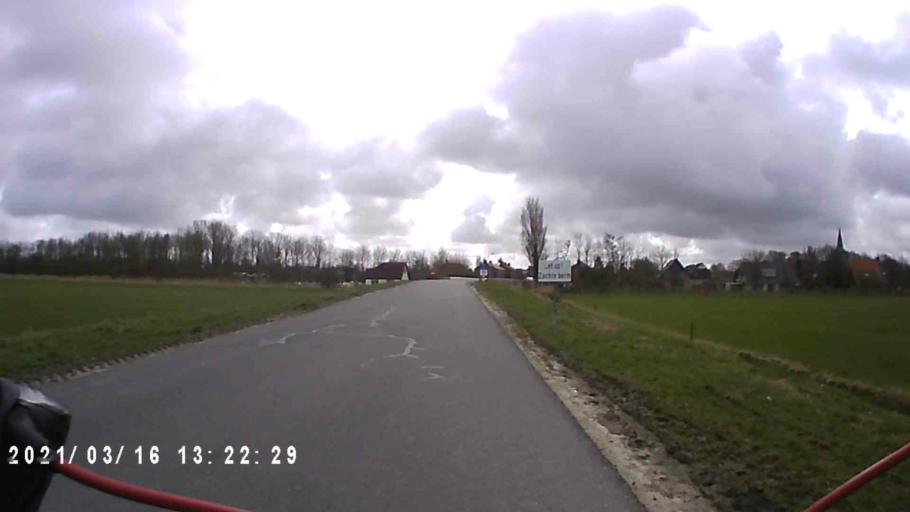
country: NL
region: Friesland
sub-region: Gemeente Het Bildt
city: Minnertsga
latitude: 53.2257
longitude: 5.5897
